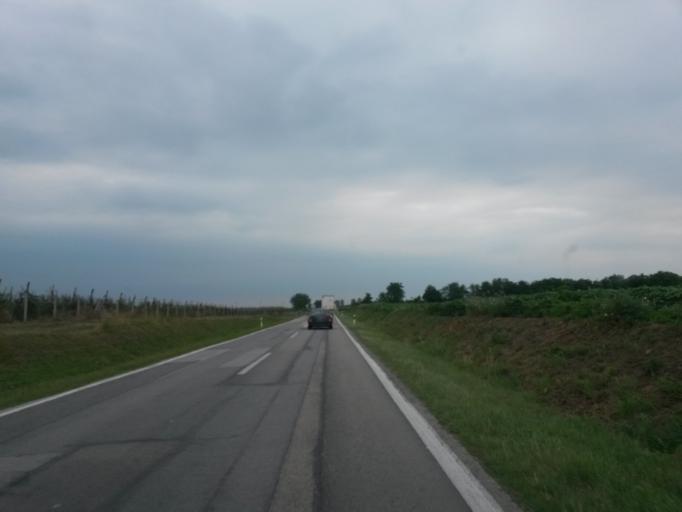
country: HR
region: Vukovarsko-Srijemska
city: Lovas
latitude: 45.2541
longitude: 19.1957
